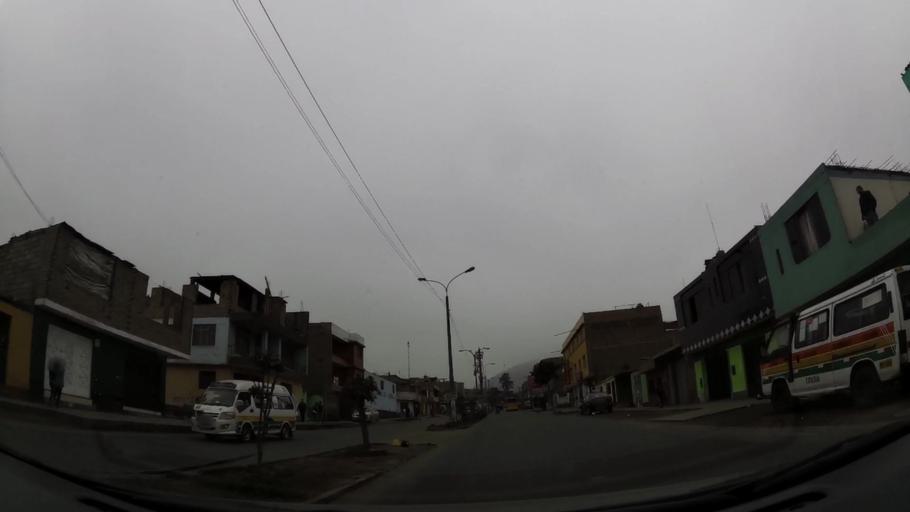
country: PE
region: Lima
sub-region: Lima
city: Urb. Santo Domingo
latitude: -11.9151
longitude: -77.0323
